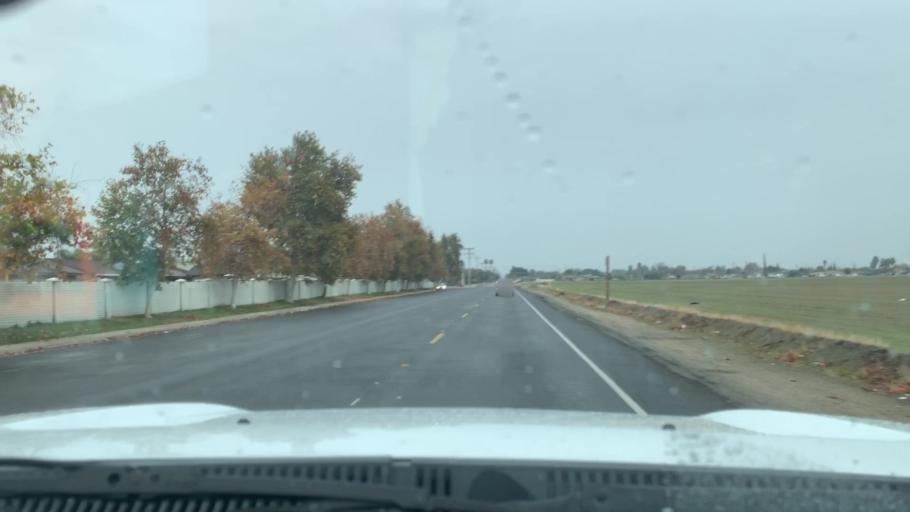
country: US
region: California
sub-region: Kern County
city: Delano
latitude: 35.7614
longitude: -119.2653
